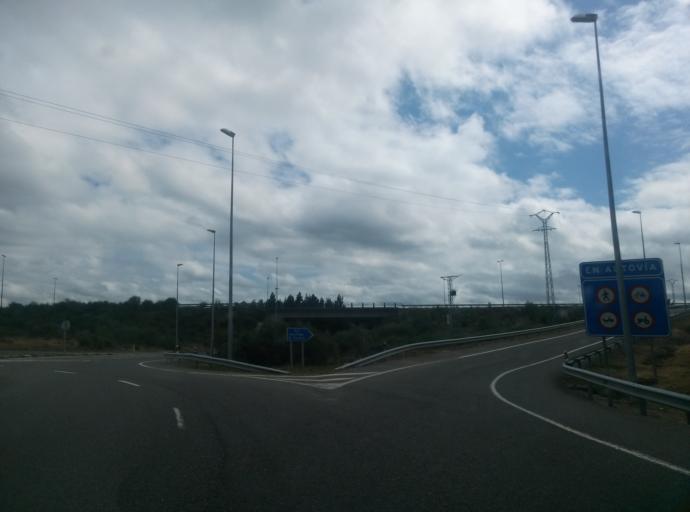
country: ES
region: Galicia
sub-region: Provincia de Lugo
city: Begonte
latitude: 43.1815
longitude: -7.7543
